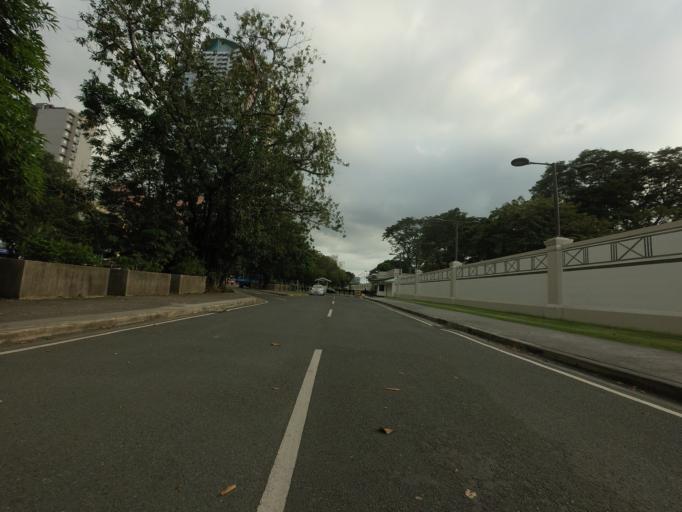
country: PH
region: Metro Manila
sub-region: City of Manila
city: Port Area
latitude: 14.5779
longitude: 120.9781
